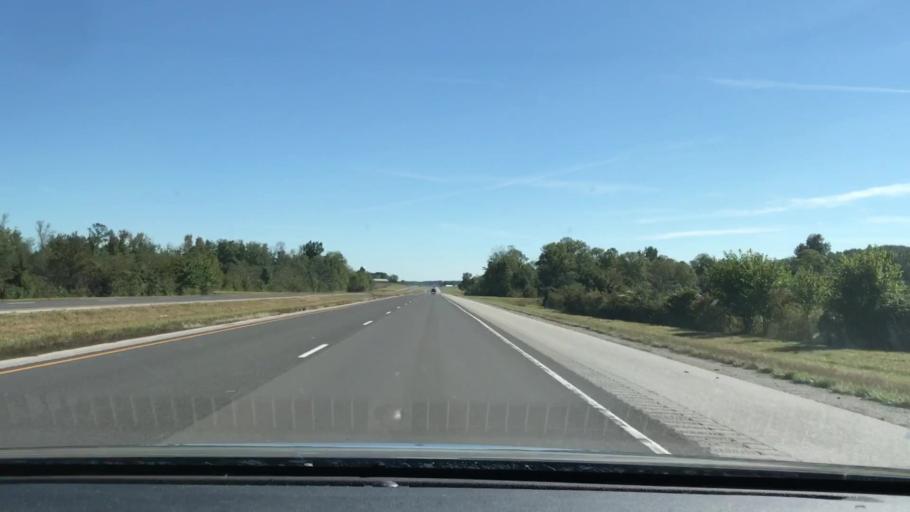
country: US
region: Kentucky
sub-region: Todd County
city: Elkton
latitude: 36.8035
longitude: -87.0796
